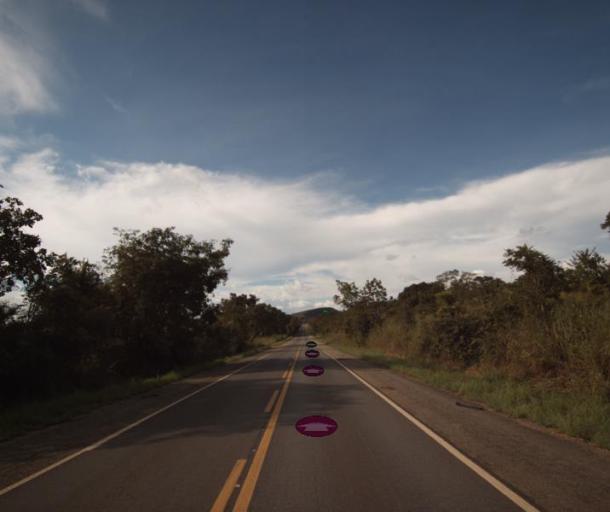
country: BR
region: Goias
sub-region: Barro Alto
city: Barro Alto
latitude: -14.9932
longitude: -48.6819
